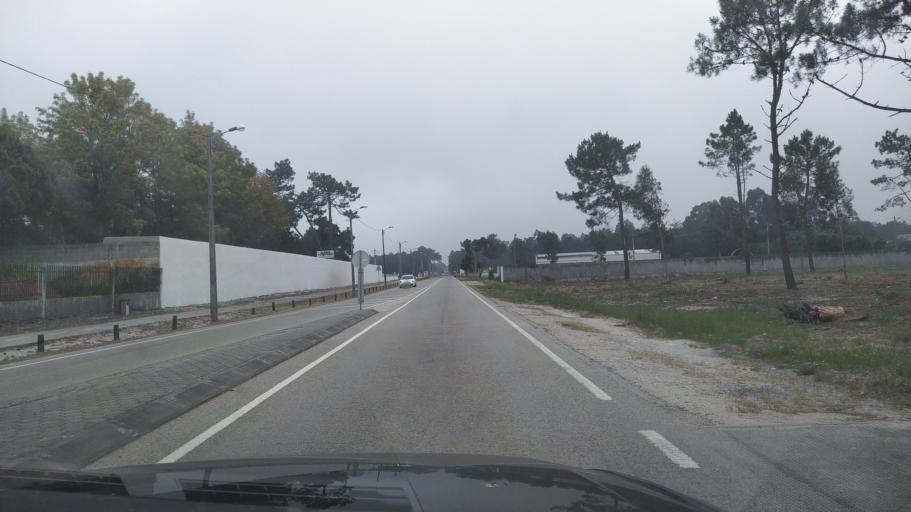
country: PT
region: Aveiro
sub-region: Ilhavo
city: Gafanha da Encarnacao
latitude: 40.6107
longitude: -8.7207
